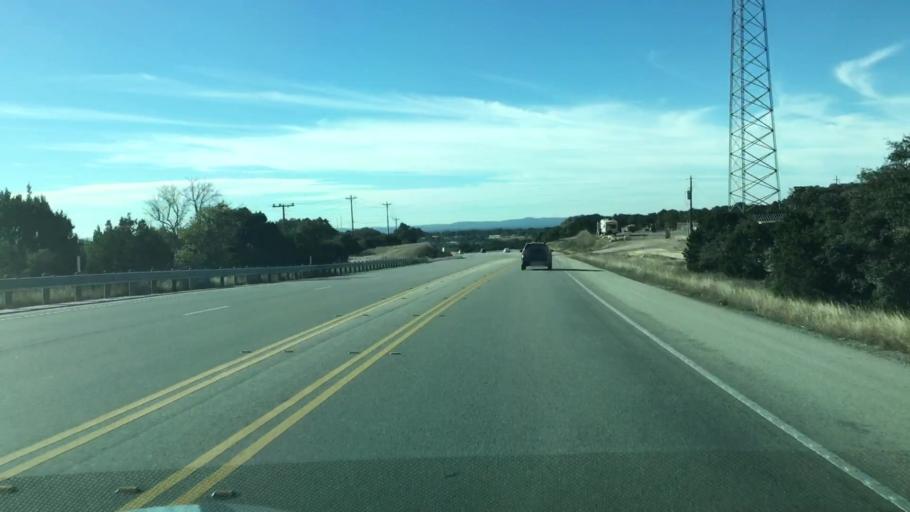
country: US
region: Texas
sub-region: Blanco County
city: Blanco
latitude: 29.9610
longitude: -98.4099
